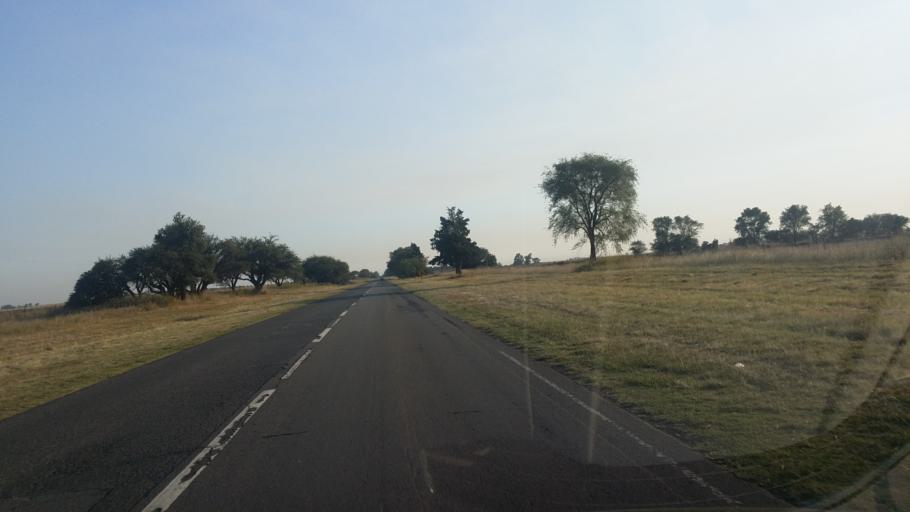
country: AR
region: La Pampa
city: Winifreda
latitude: -36.2135
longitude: -64.2782
